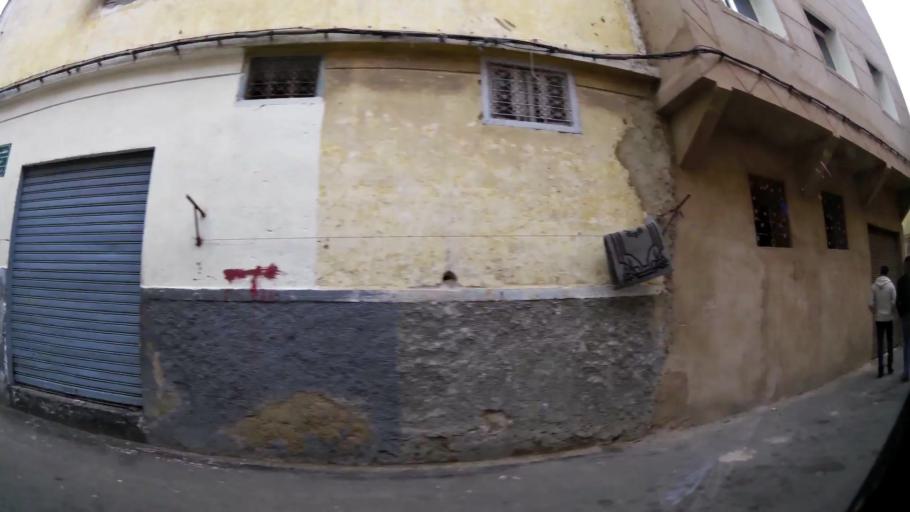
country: MA
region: Grand Casablanca
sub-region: Casablanca
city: Casablanca
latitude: 33.5638
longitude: -7.5639
